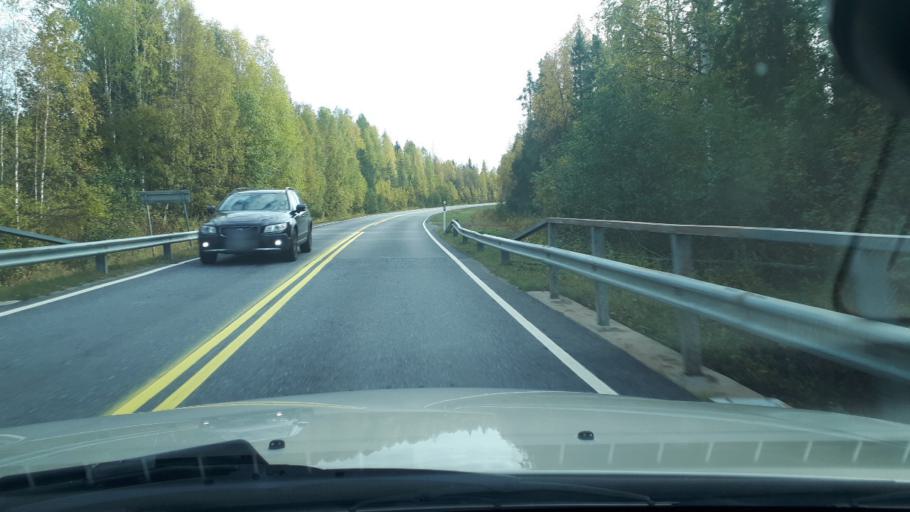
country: FI
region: Lapland
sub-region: Rovaniemi
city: Ranua
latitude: 65.9682
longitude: 26.0108
